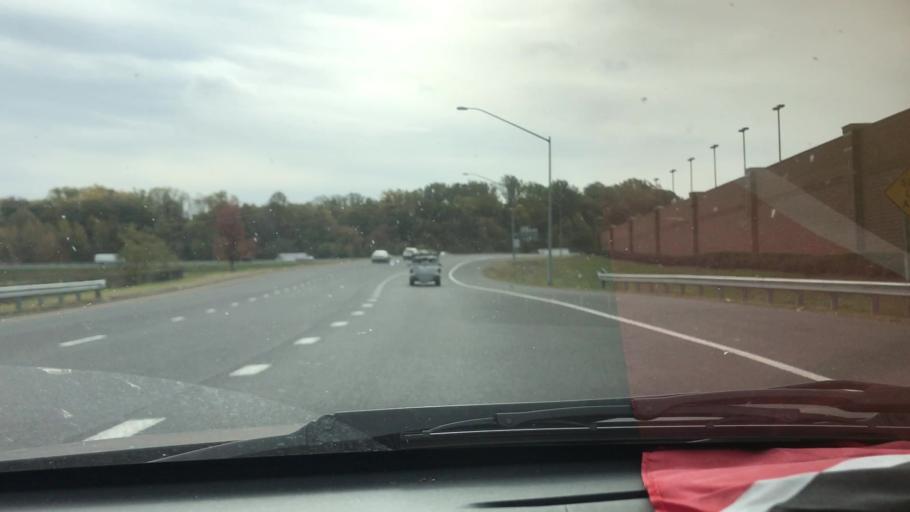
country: US
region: Maryland
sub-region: Prince George's County
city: Largo
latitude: 38.8679
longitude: -76.8474
